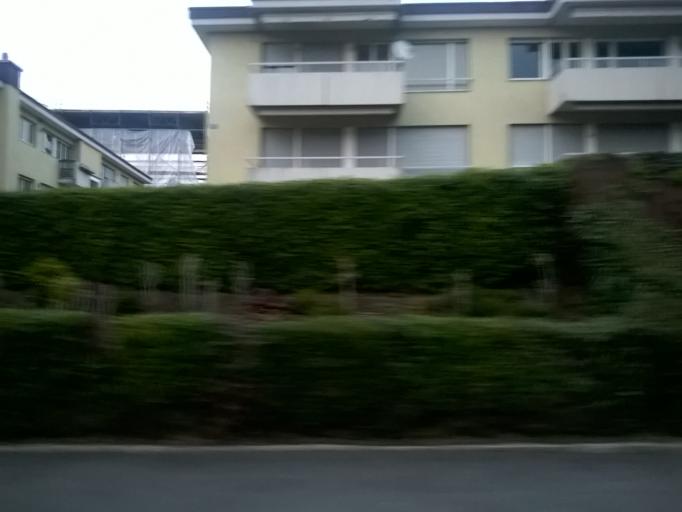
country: CH
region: Zurich
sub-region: Bezirk Buelach
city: Wallisellen / Wallisellen-Ost
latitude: 47.4116
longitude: 8.5977
